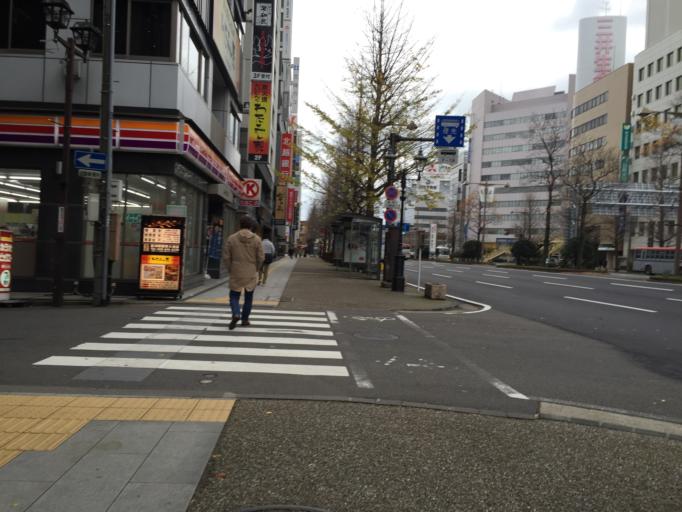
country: JP
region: Niigata
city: Niigata-shi
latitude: 37.9139
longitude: 139.0608
